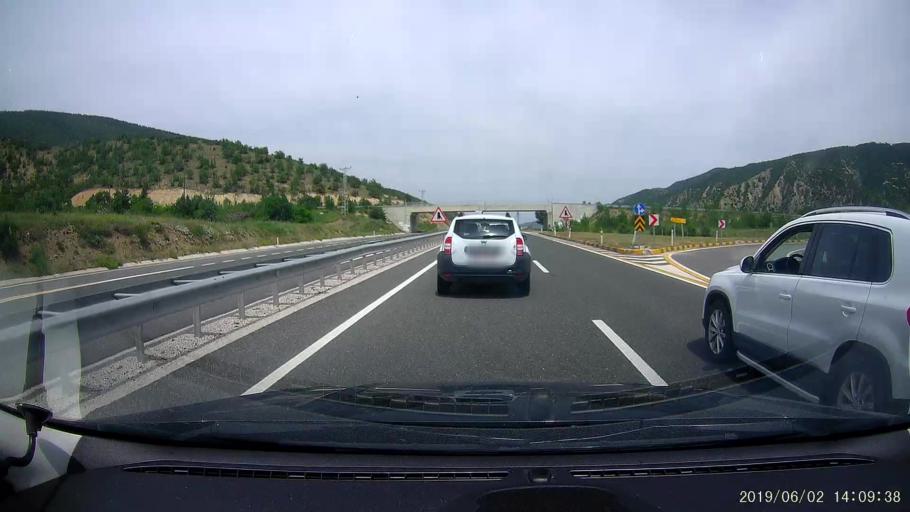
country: TR
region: Cankiri
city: Ilgaz
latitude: 40.8965
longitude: 33.7450
